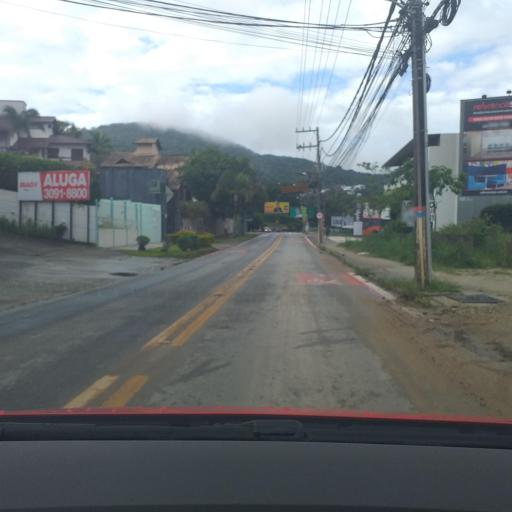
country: BR
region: Santa Catarina
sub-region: Florianopolis
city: Corrego Grande
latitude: -27.5987
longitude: -48.4988
